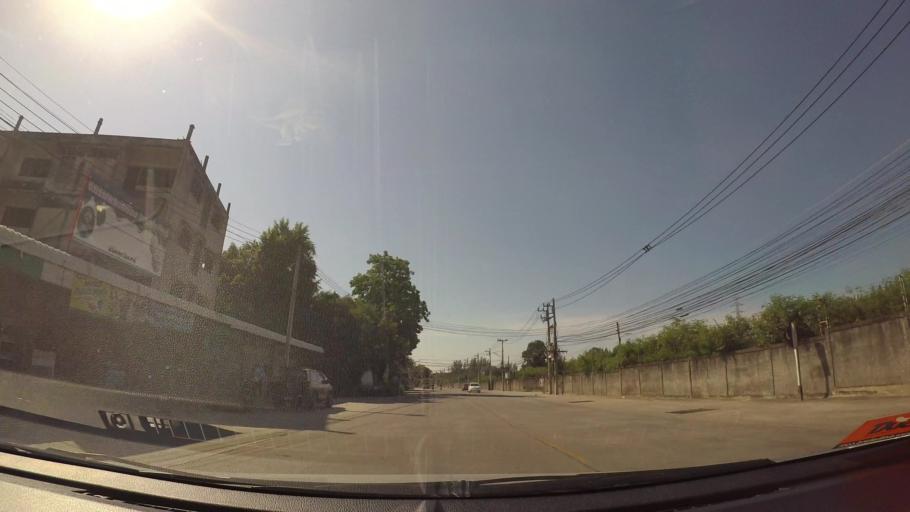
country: TH
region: Chon Buri
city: Si Racha
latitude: 13.1571
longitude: 100.9413
